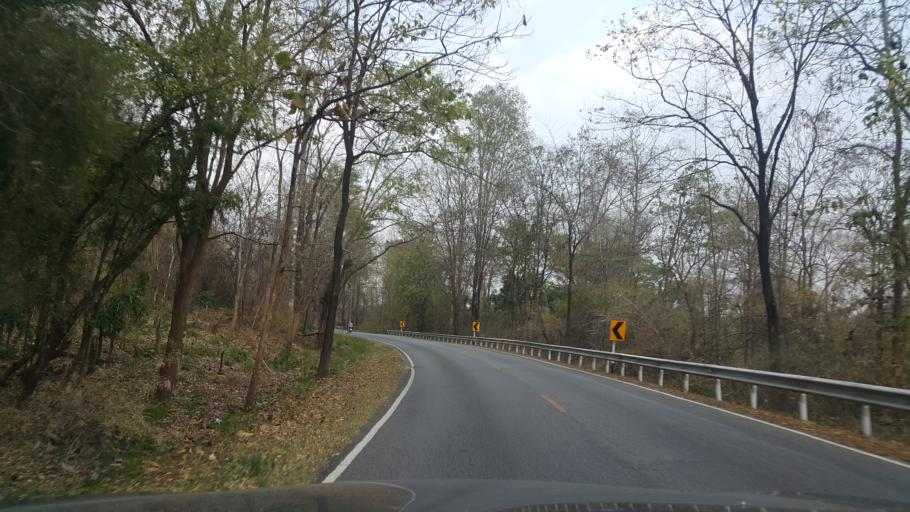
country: TH
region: Lamphun
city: Thung Hua Chang
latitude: 17.9596
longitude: 99.1532
